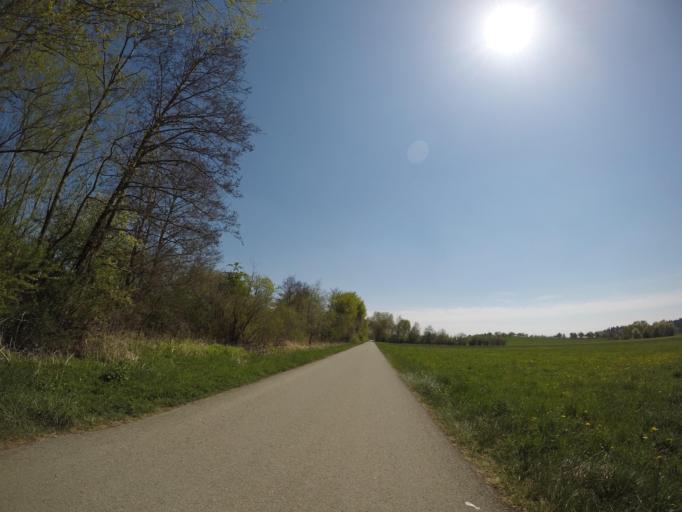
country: DE
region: Baden-Wuerttemberg
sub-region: Tuebingen Region
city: Markdorf
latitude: 47.7094
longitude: 9.3927
